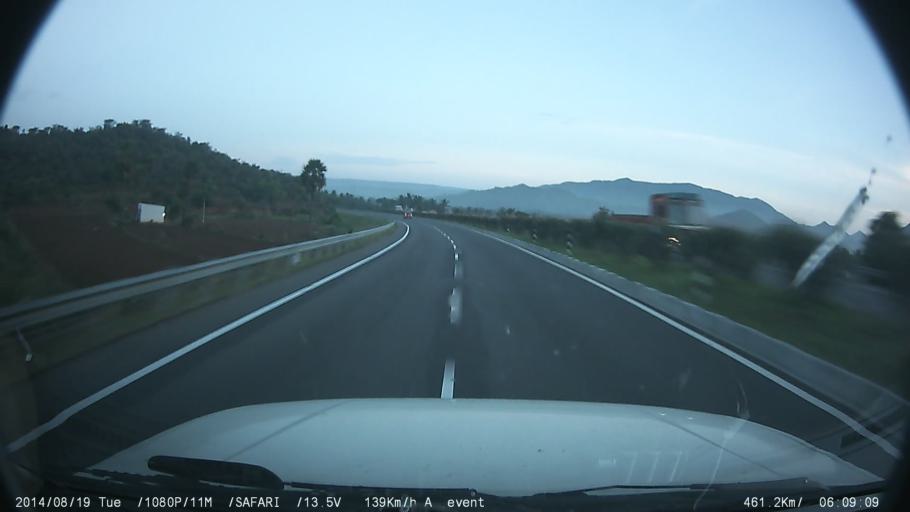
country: IN
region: Tamil Nadu
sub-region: Dharmapuri
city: Mallapuram
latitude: 11.9311
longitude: 78.0649
